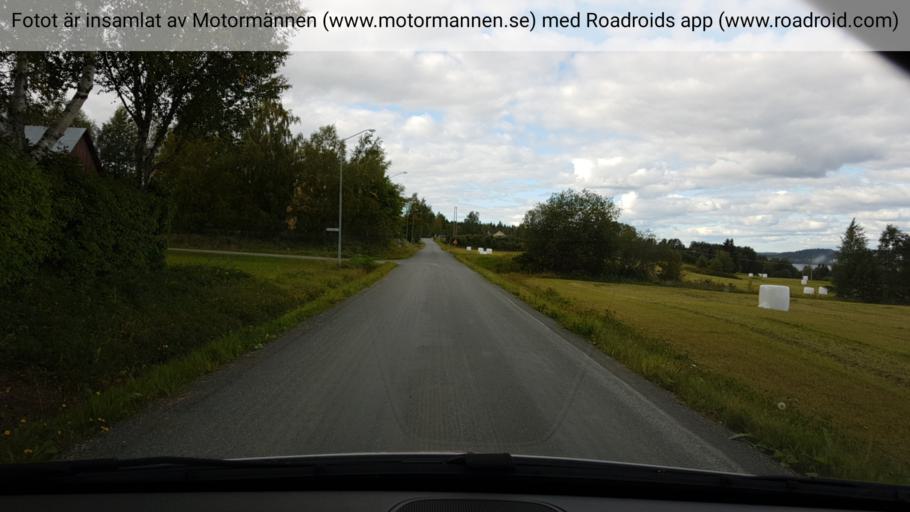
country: SE
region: Jaemtland
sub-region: OEstersunds Kommun
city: Ostersund
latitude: 63.1295
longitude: 14.6456
